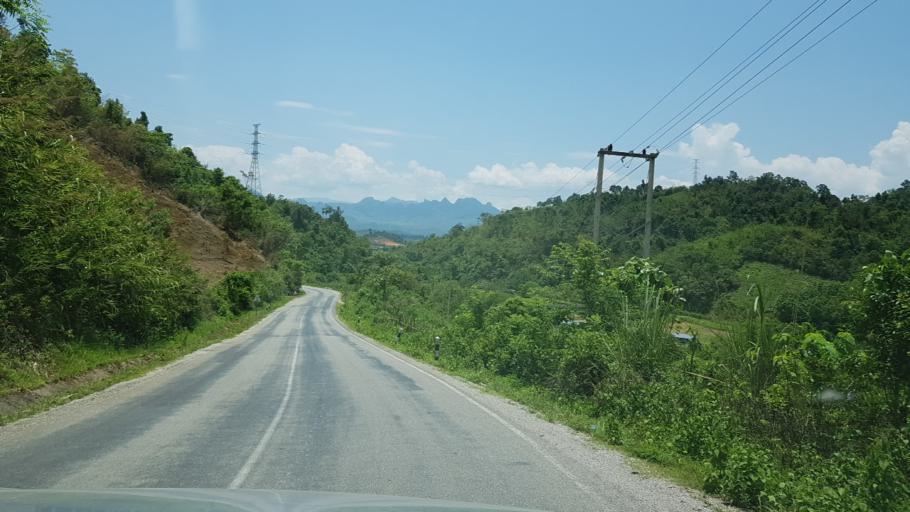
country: LA
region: Vientiane
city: Muang Kasi
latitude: 19.2715
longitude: 102.2072
